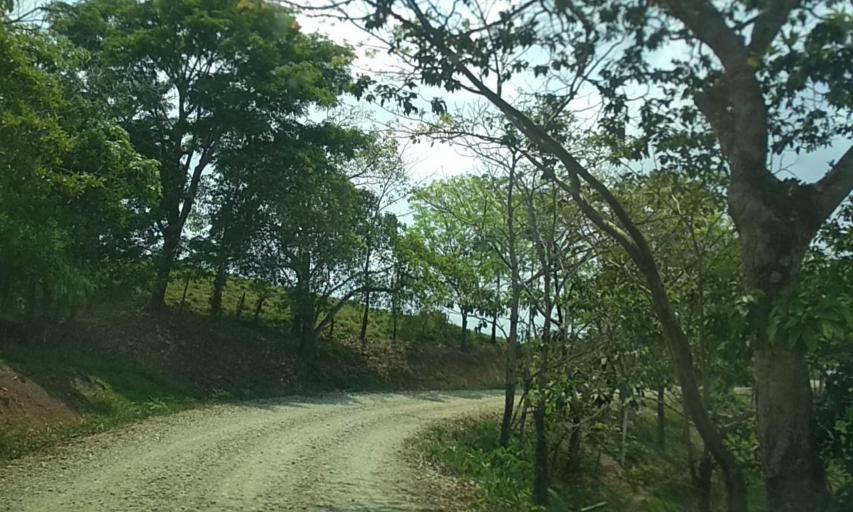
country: MX
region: Tabasco
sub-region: Huimanguillo
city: Francisco Rueda
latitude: 17.6227
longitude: -93.8171
